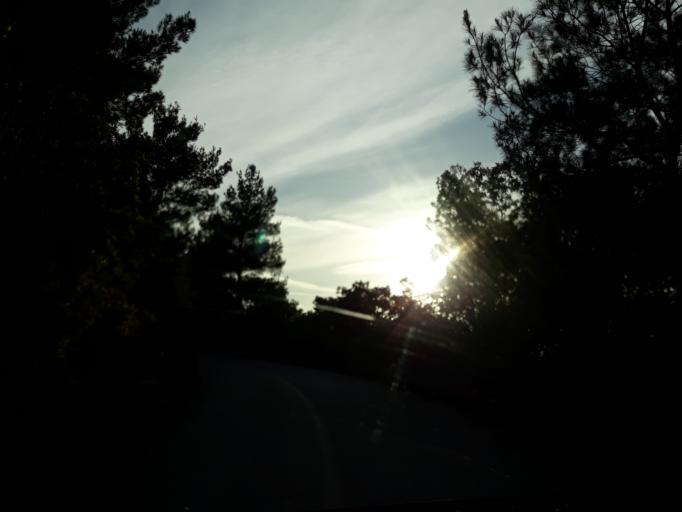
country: GR
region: Attica
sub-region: Nomarchia Anatolikis Attikis
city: Afidnes
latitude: 38.2268
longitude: 23.7945
